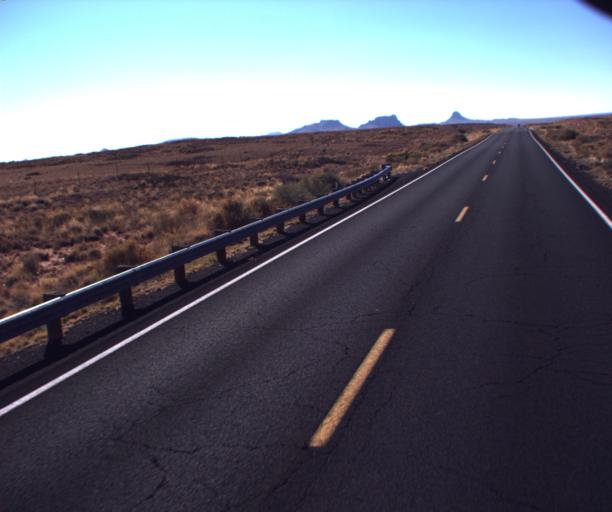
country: US
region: Arizona
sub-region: Navajo County
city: Dilkon
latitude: 35.4079
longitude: -110.4265
